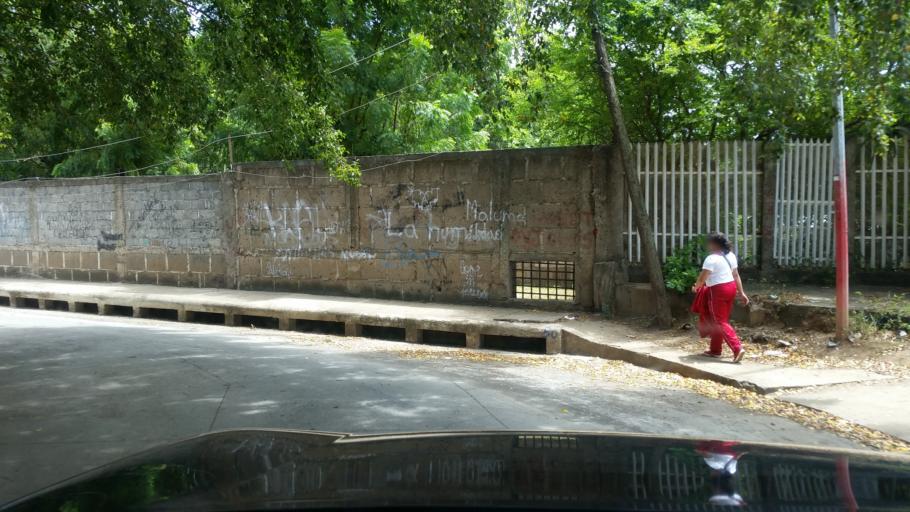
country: NI
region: Managua
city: Managua
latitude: 12.1187
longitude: -86.2209
